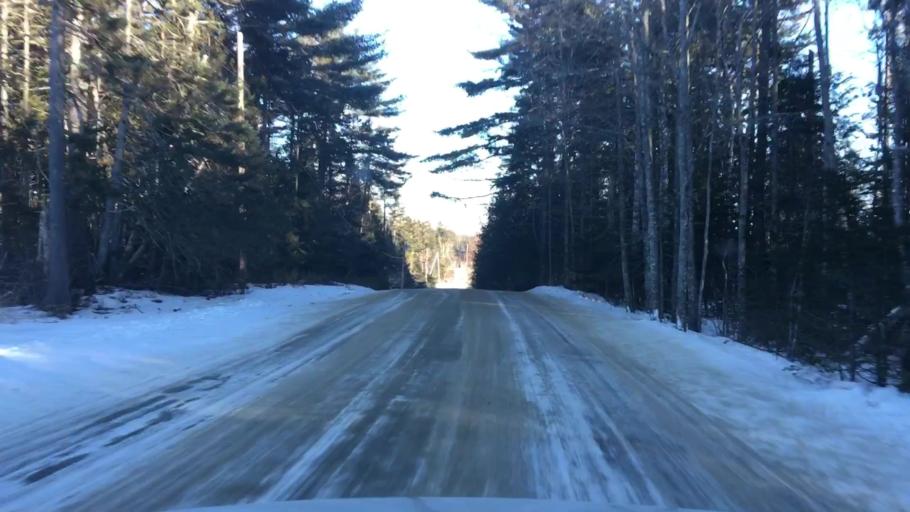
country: US
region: Maine
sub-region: Hancock County
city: Castine
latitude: 44.3823
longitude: -68.7302
